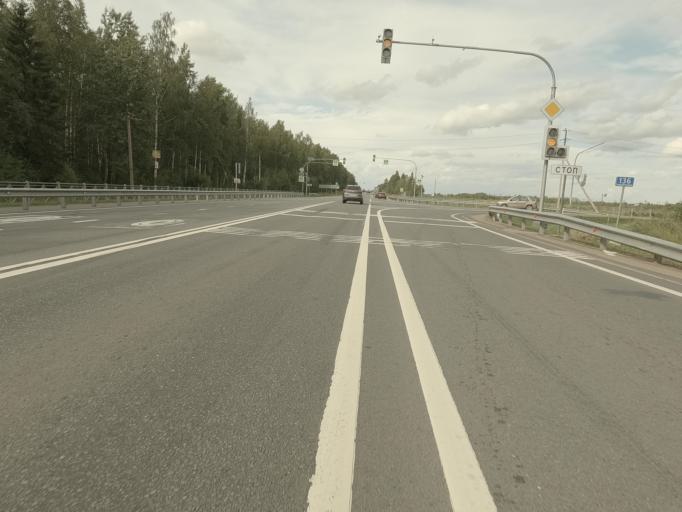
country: RU
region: Leningrad
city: Mga
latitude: 59.7841
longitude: 31.1052
